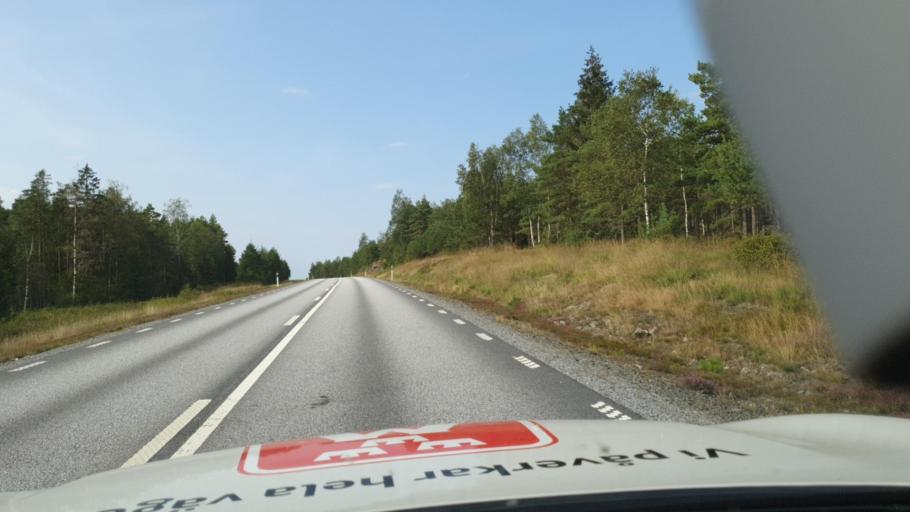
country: SE
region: Vaestra Goetaland
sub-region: Dals-Ed Kommun
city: Ed
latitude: 58.8403
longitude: 11.6294
